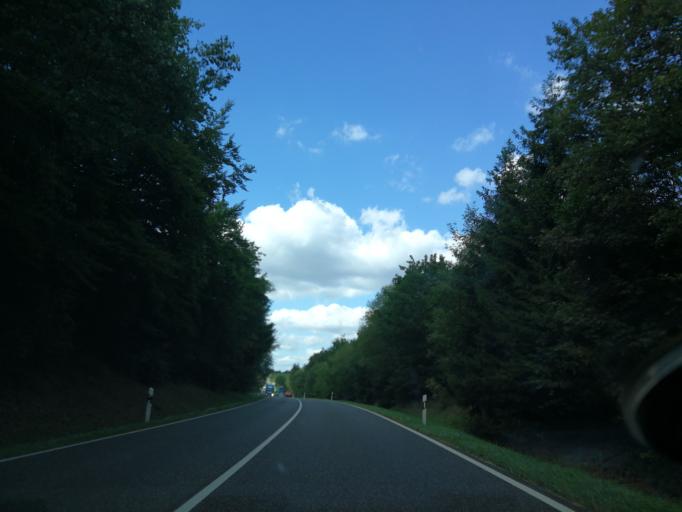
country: DE
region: North Rhine-Westphalia
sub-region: Regierungsbezirk Koln
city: Blankenheim
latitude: 50.4566
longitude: 6.7037
